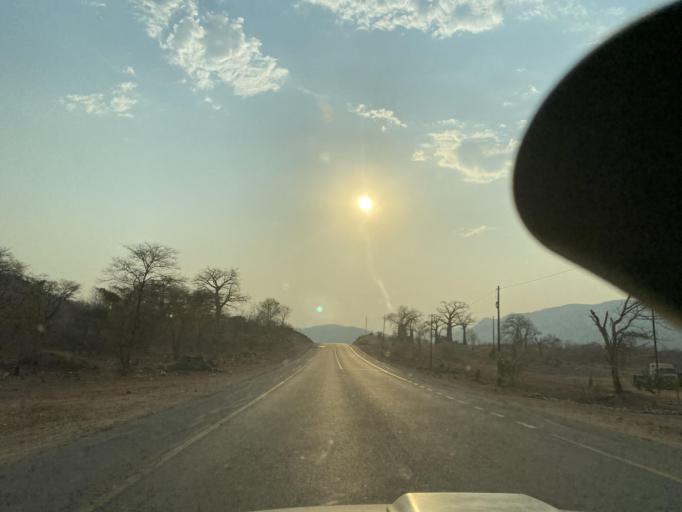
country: ZW
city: Chirundu
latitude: -16.0187
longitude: 28.6210
